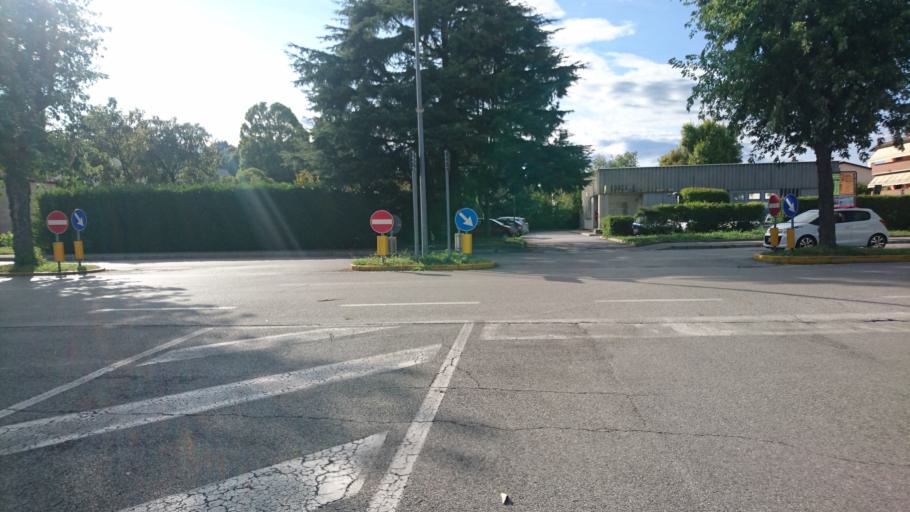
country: IT
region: Veneto
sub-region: Provincia di Padova
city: Albignasego
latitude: 45.3465
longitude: 11.8702
